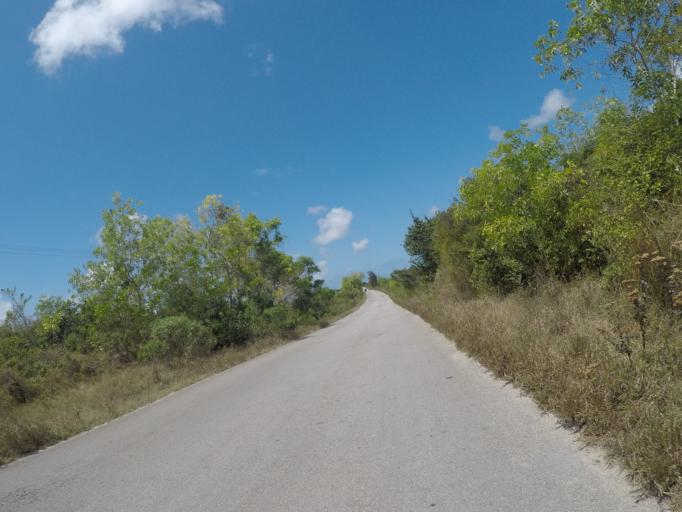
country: TZ
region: Zanzibar Central/South
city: Nganane
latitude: -6.2859
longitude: 39.4520
